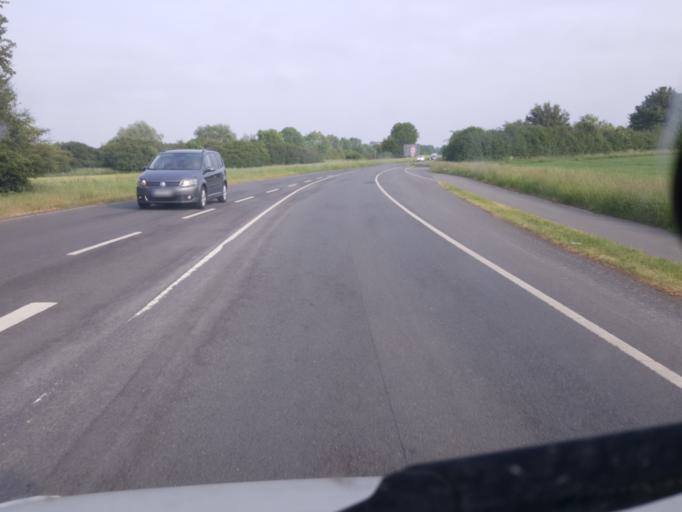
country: DE
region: Lower Saxony
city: Marklohe
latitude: 52.6542
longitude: 9.1874
